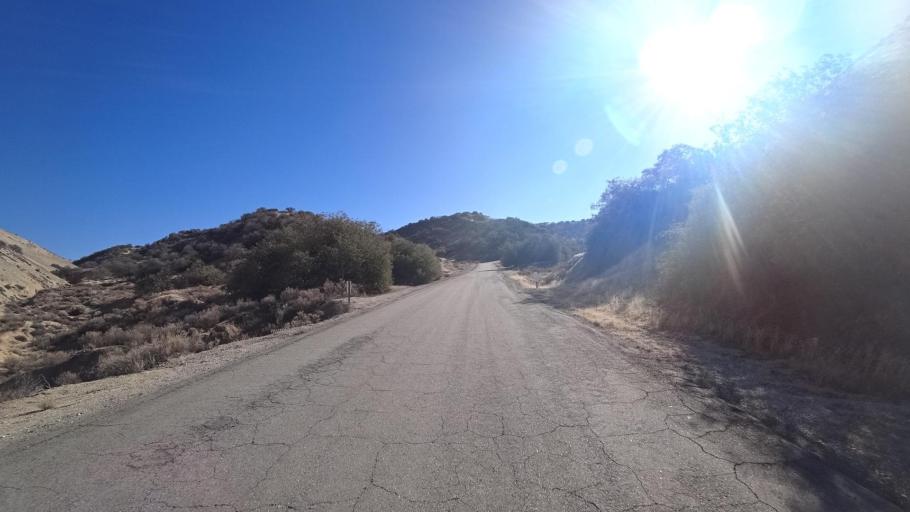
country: US
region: California
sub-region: Kern County
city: Maricopa
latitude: 34.9473
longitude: -119.4015
